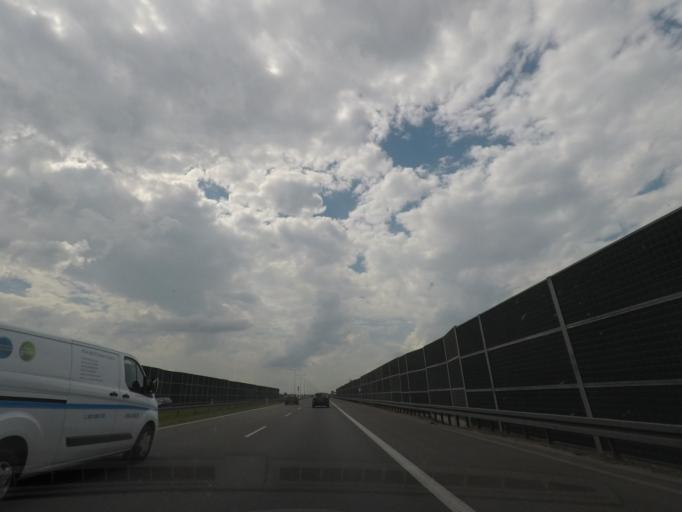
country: PL
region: Masovian Voivodeship
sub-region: Powiat pruszkowski
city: Brwinow
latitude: 52.1582
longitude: 20.6997
